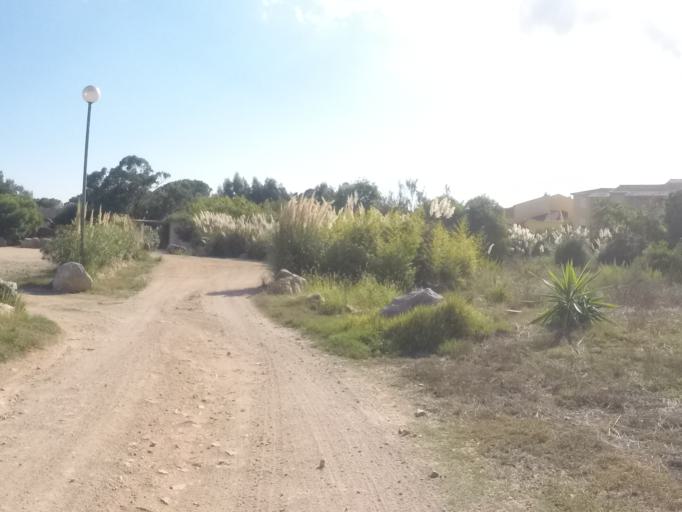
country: FR
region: Corsica
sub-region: Departement de la Corse-du-Sud
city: Porto-Vecchio
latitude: 41.6096
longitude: 9.2866
